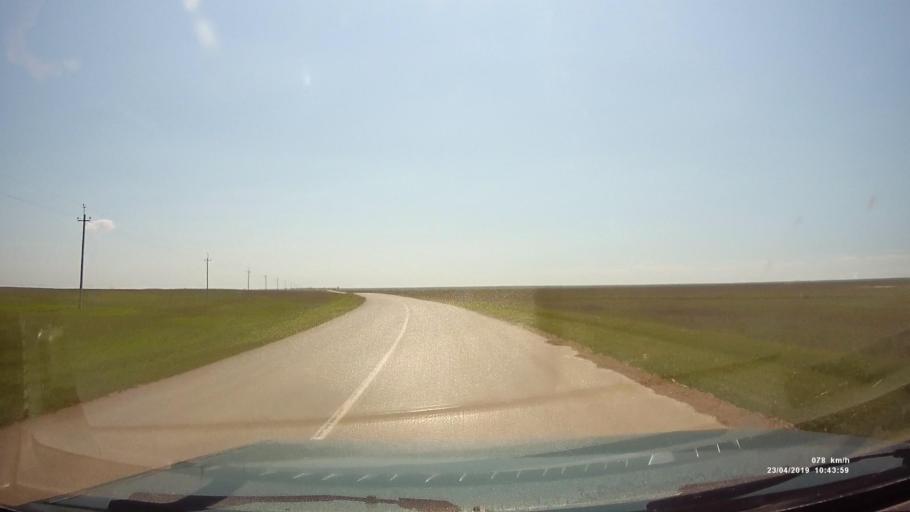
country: RU
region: Kalmykiya
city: Yashalta
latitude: 46.4634
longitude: 42.6509
